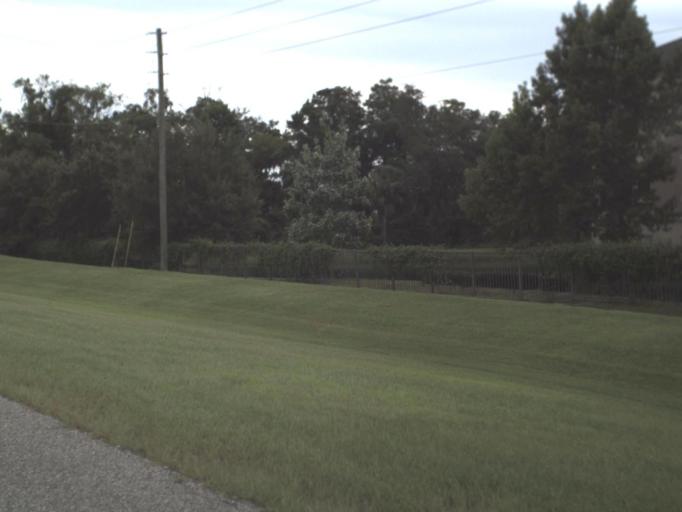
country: US
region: Florida
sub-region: Hillsborough County
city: Pebble Creek
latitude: 28.1856
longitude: -82.3576
